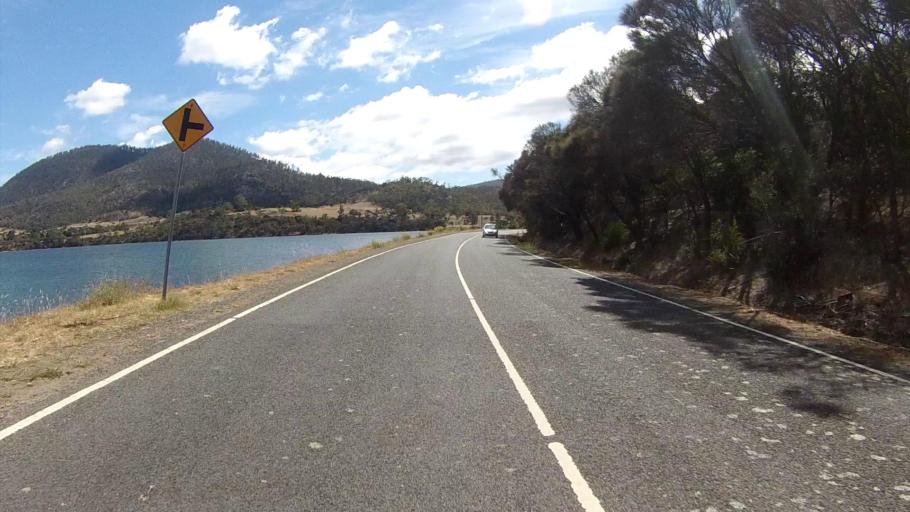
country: AU
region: Tasmania
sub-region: Glenorchy
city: Lutana
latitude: -42.8220
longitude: 147.3180
